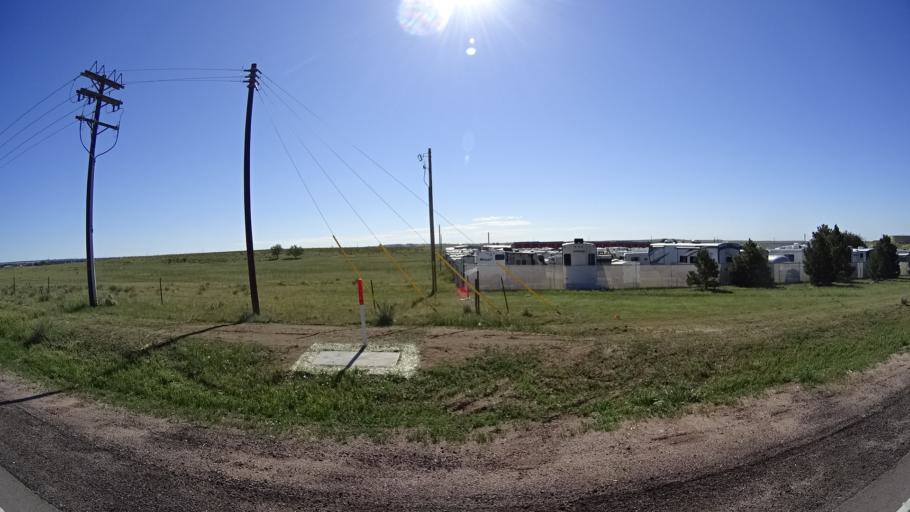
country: US
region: Colorado
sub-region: El Paso County
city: Cimarron Hills
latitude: 38.9086
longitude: -104.6829
